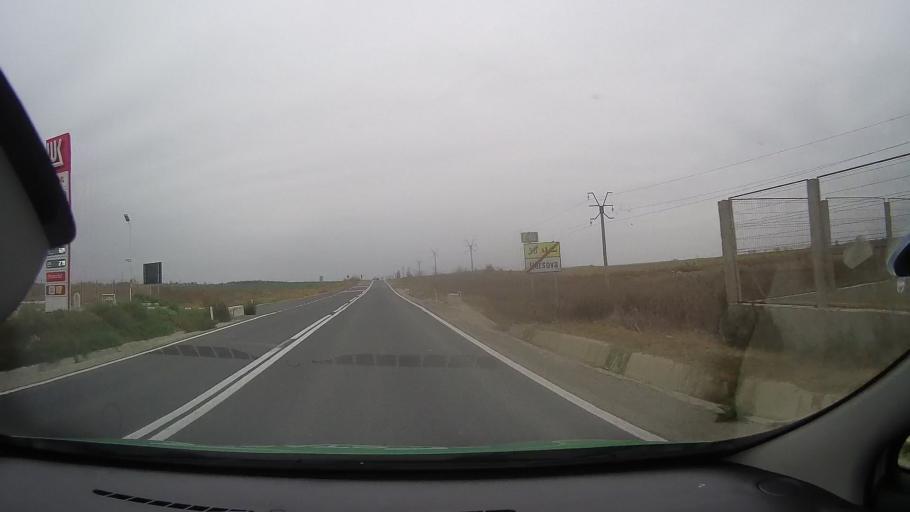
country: RO
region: Constanta
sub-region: Oras Harsova
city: Harsova
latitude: 44.6920
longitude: 27.9393
